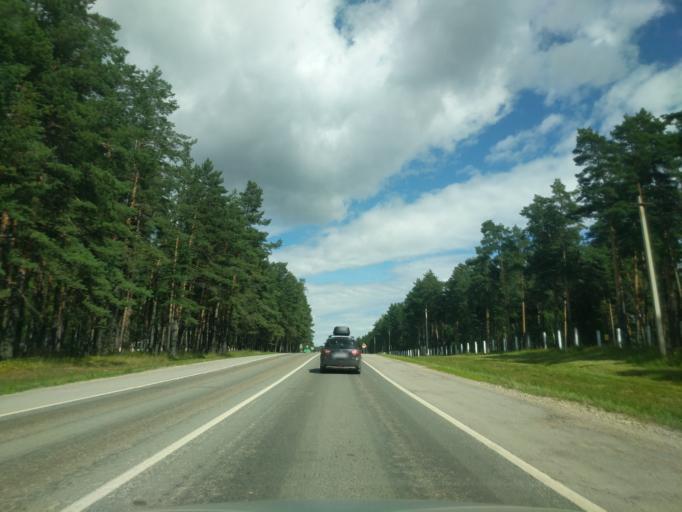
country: RU
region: Jaroslavl
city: Levashevo
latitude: 57.6739
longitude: 40.5851
